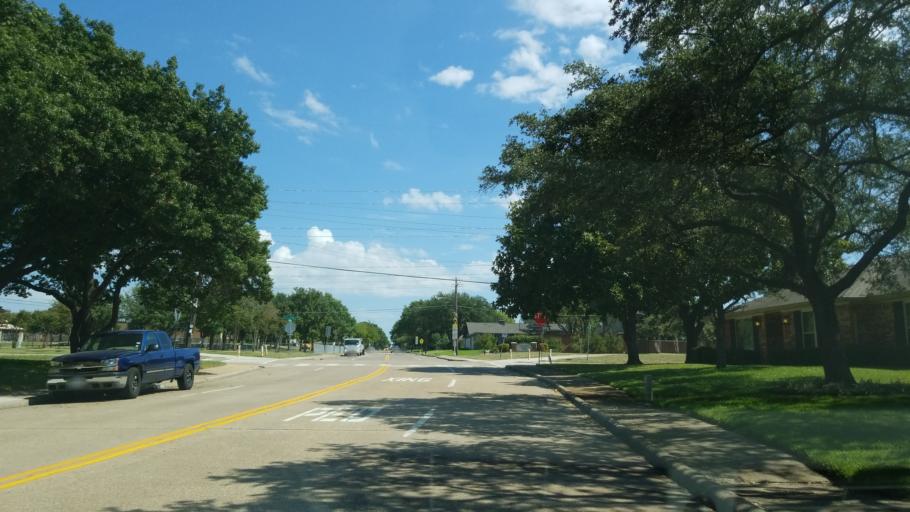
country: US
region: Texas
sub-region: Dallas County
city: Addison
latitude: 32.9704
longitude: -96.7791
